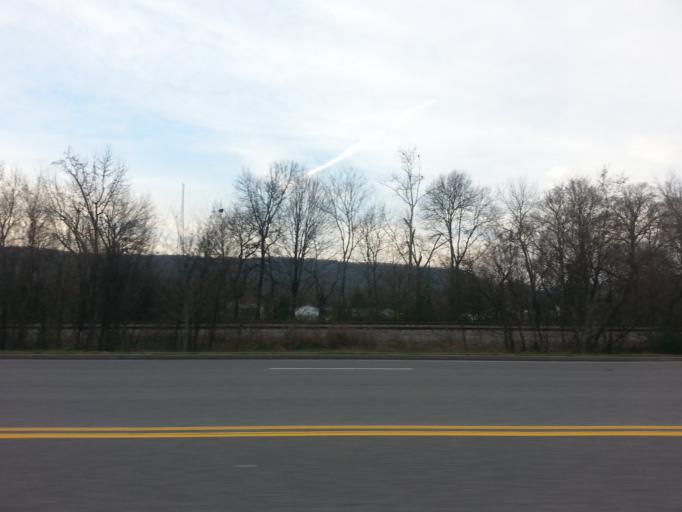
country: US
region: Tennessee
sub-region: Rhea County
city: Spring City
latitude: 35.6885
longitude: -84.8635
